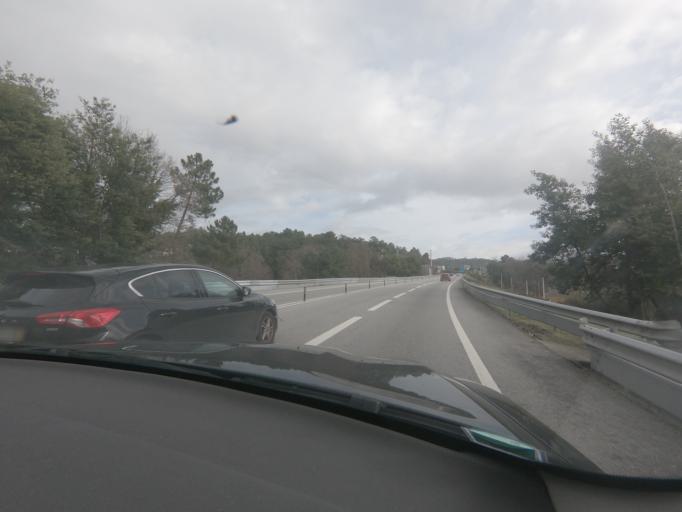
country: PT
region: Vila Real
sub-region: Vila Real
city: Vila Real
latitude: 41.3167
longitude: -7.7126
